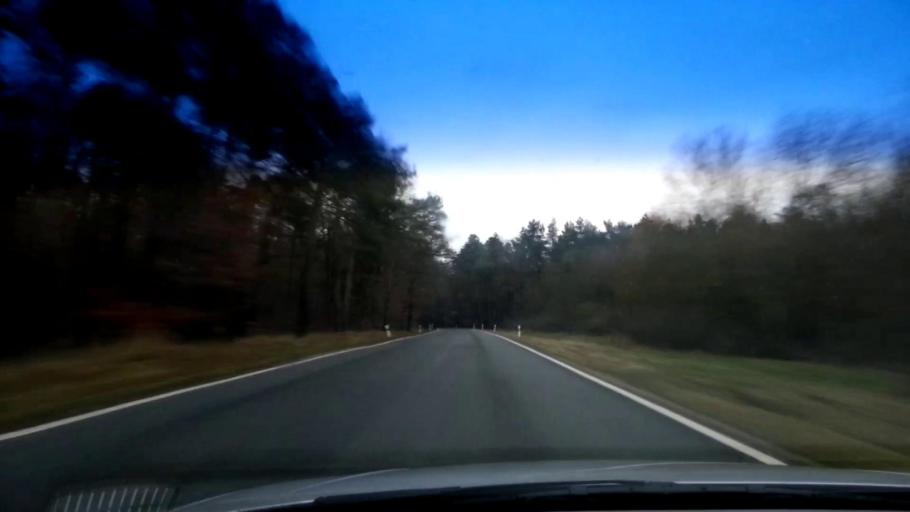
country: DE
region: Bavaria
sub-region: Regierungsbezirk Mittelfranken
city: Muhlhausen
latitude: 49.7952
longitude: 10.7856
